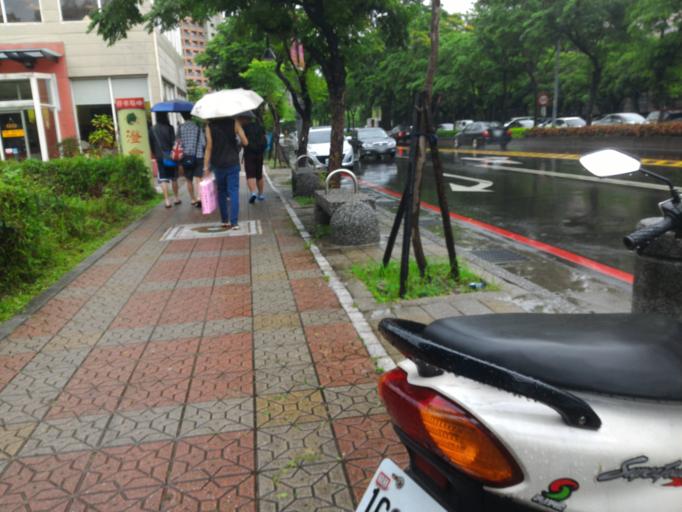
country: TW
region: Taiwan
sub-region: Taoyuan
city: Taoyuan
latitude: 24.9393
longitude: 121.3683
